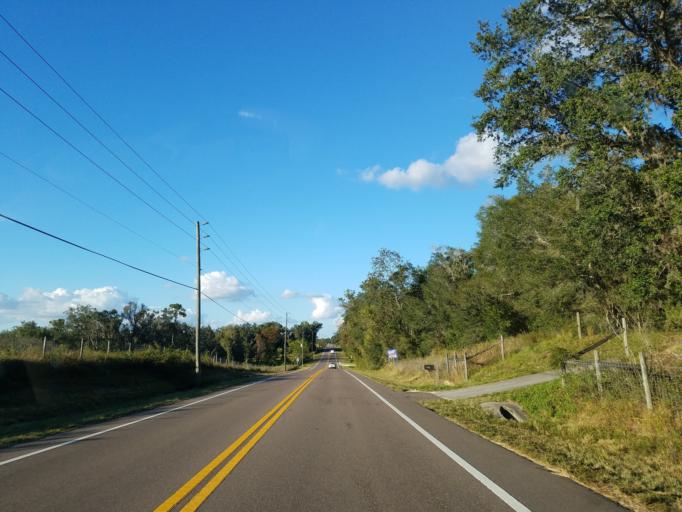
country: US
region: Florida
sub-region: Hernando County
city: Hill 'n Dale
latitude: 28.4407
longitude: -82.3028
